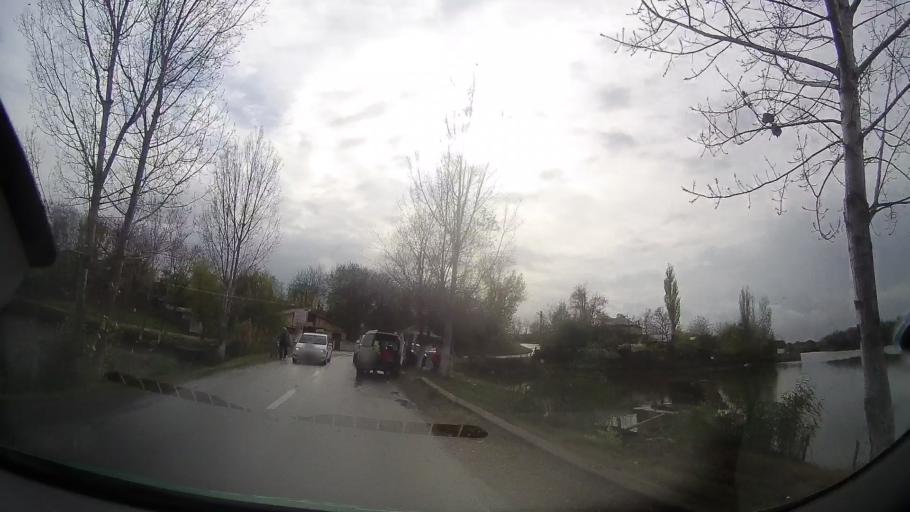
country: RO
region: Ialomita
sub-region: Comuna Maia
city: Maia
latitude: 44.7342
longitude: 26.4015
